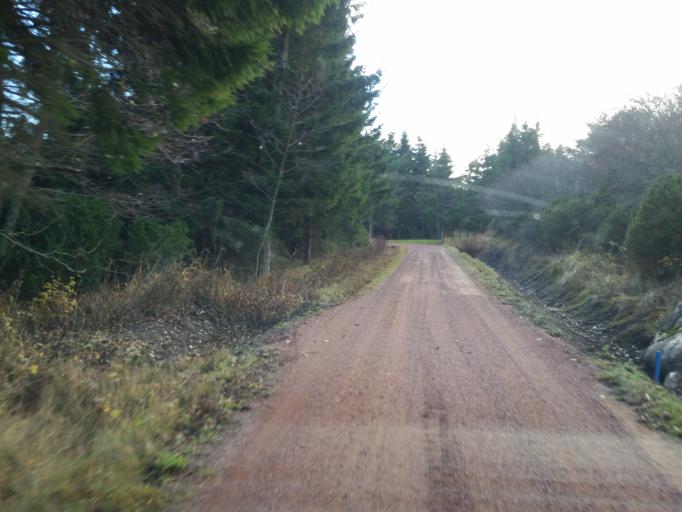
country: AX
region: Alands skaergard
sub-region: Kumlinge
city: Kumlinge
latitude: 60.2522
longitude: 20.7572
